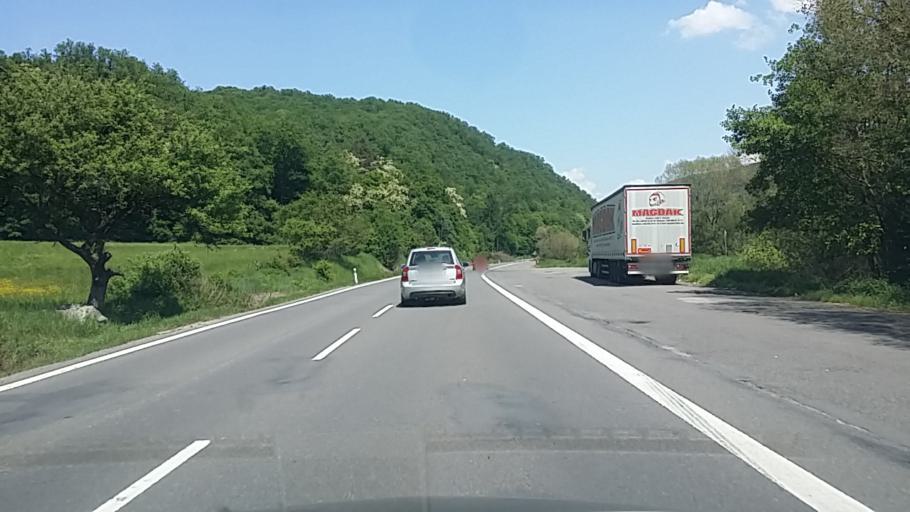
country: SK
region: Banskobystricky
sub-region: Okres Banska Bystrica
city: Zvolen
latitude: 48.5253
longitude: 19.1070
